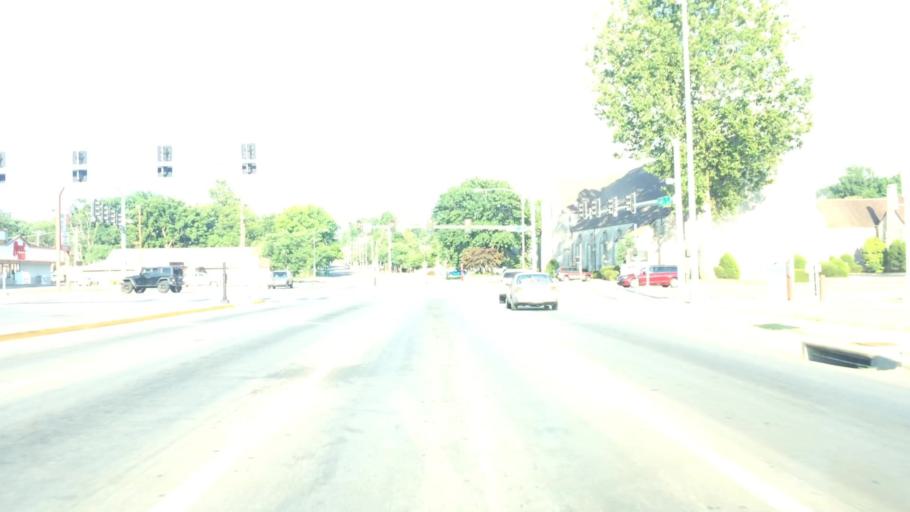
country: US
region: Missouri
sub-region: Greene County
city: Springfield
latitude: 37.1966
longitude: -93.2769
